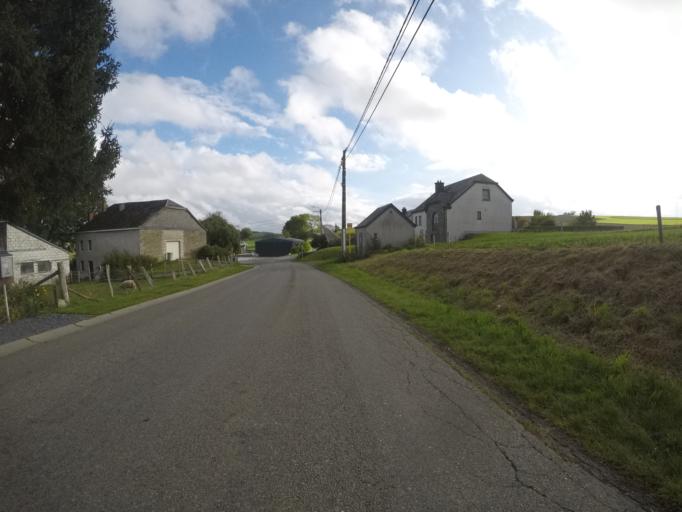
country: BE
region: Wallonia
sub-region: Province du Luxembourg
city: Bastogne
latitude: 49.9536
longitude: 5.6914
